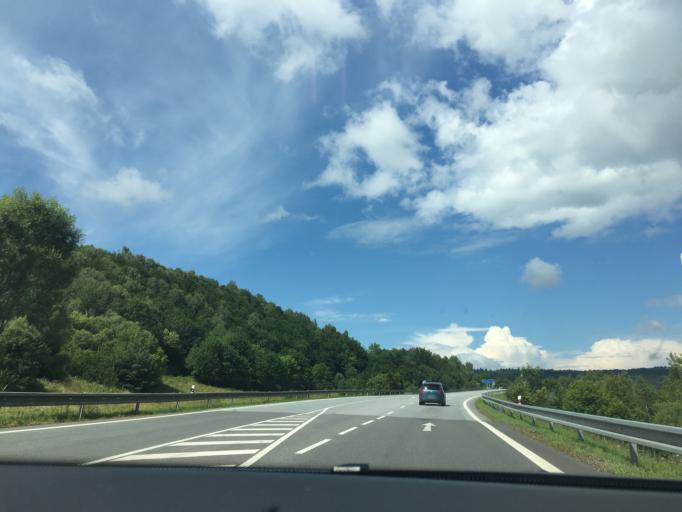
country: PL
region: Subcarpathian Voivodeship
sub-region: Powiat krosnienski
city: Jasliska
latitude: 49.3944
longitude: 21.6990
